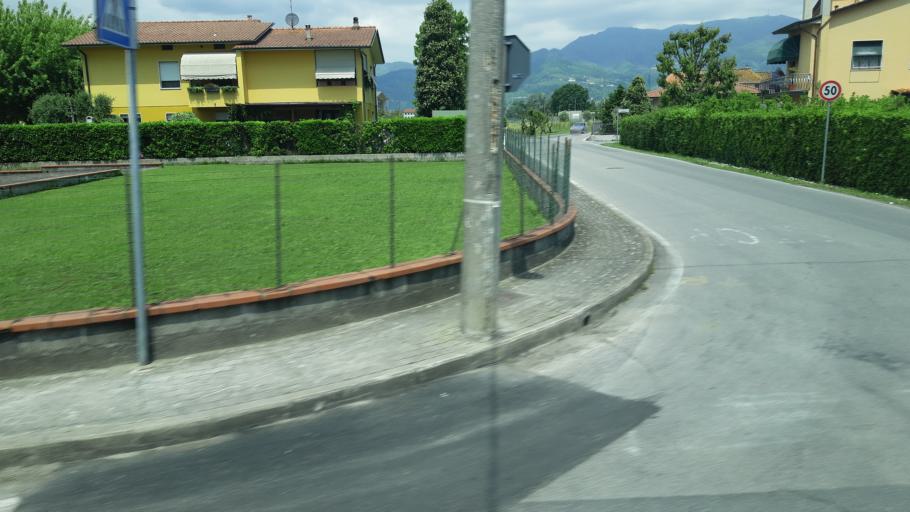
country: IT
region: Tuscany
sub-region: Provincia di Lucca
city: Capannori
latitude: 43.8699
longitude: 10.5405
